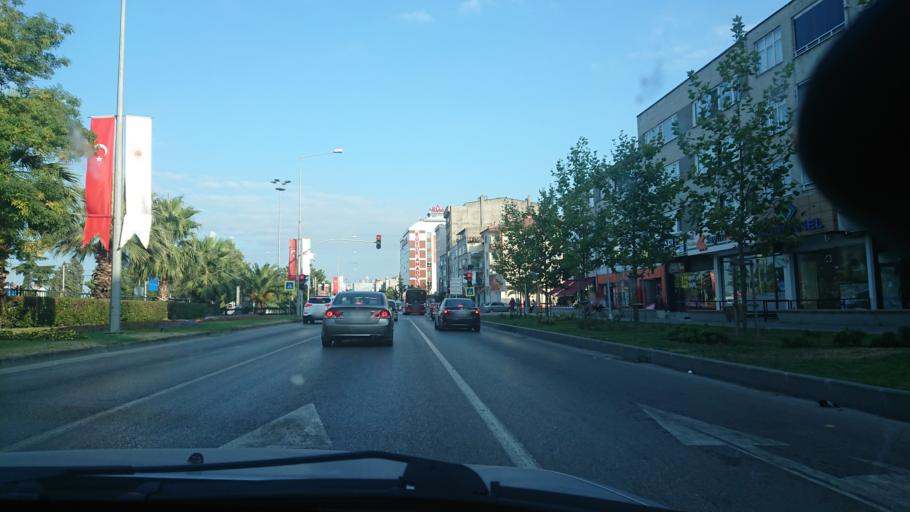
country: TR
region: Samsun
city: Samsun
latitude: 41.2860
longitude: 36.3409
